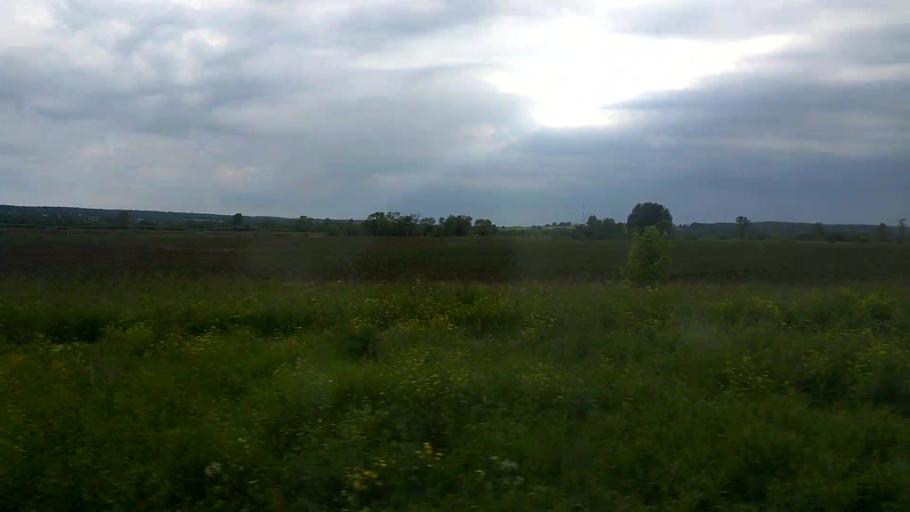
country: RU
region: Moskovskaya
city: Ozery
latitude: 54.8408
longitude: 38.5754
